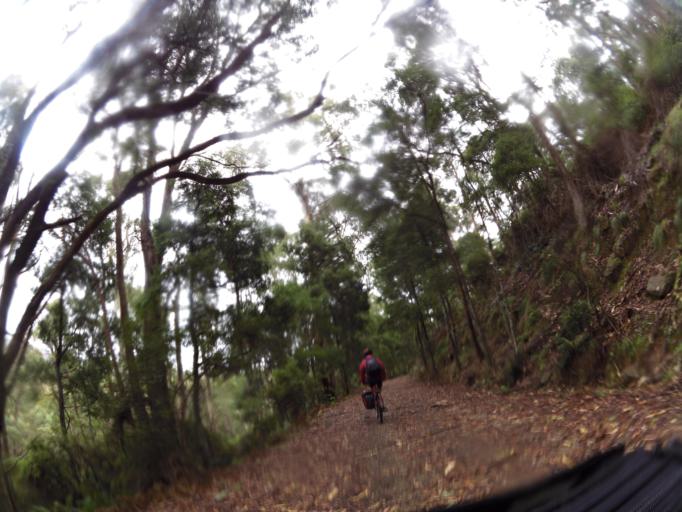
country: AU
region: New South Wales
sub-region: Greater Hume Shire
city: Holbrook
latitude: -36.1942
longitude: 147.5129
